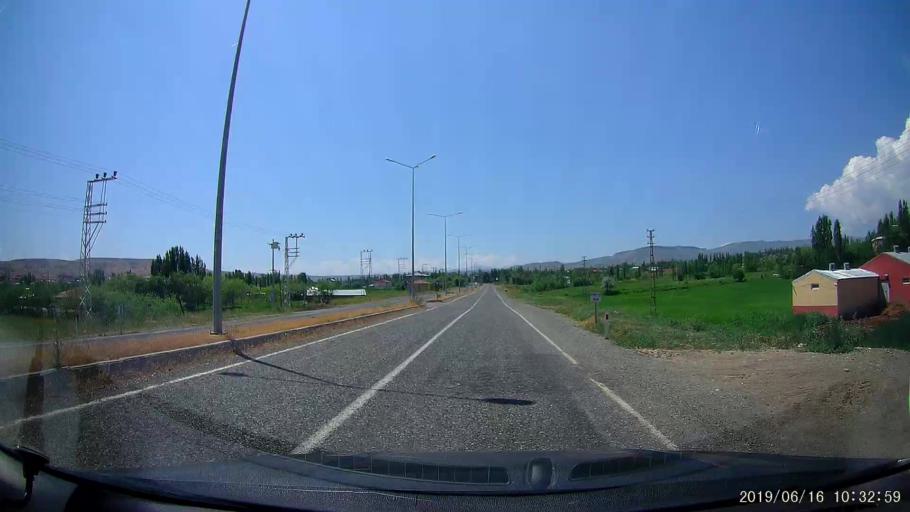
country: TR
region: Igdir
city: Tuzluca
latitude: 40.0452
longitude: 43.6545
